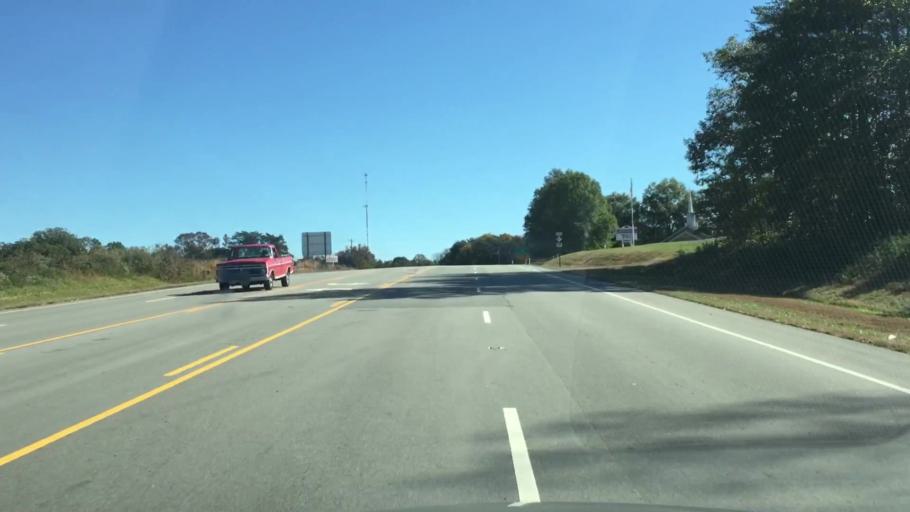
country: US
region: North Carolina
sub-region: Rockingham County
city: Reidsville
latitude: 36.3129
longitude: -79.6352
